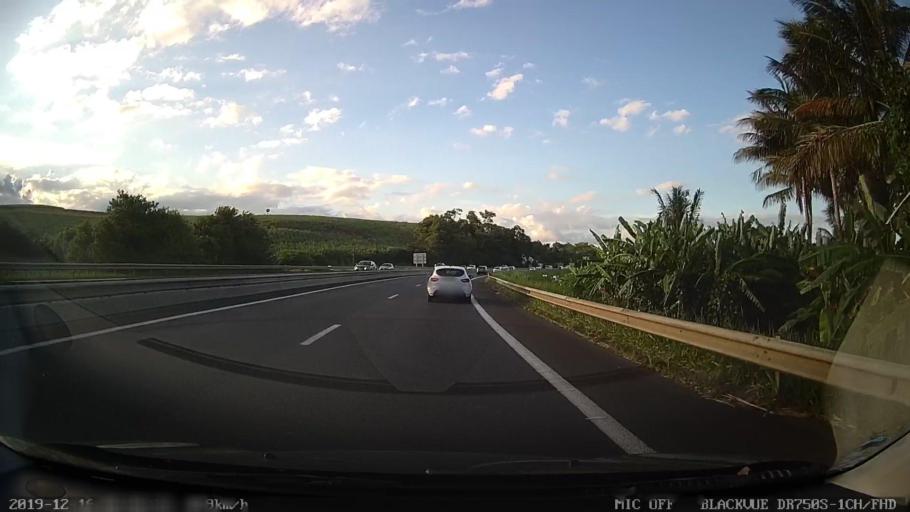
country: RE
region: Reunion
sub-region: Reunion
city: Sainte-Suzanne
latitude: -20.9258
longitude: 55.6294
